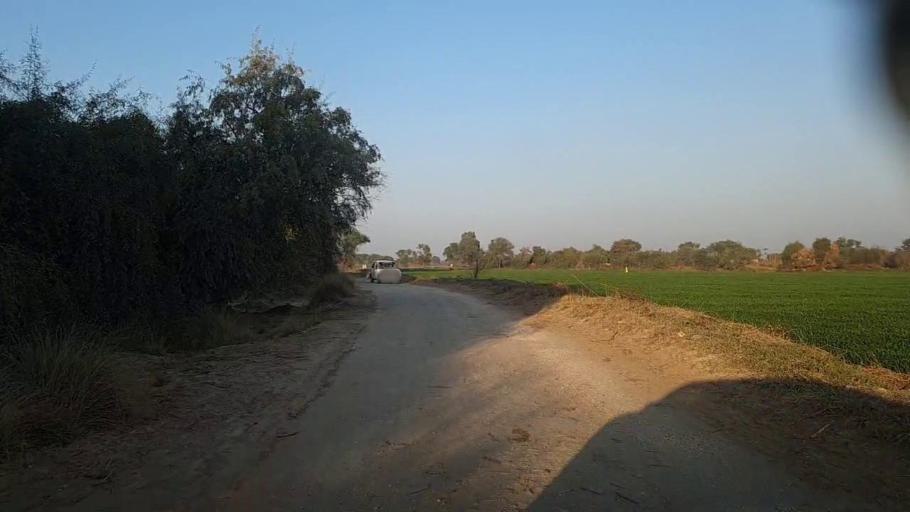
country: PK
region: Sindh
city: Mirpur Mathelo
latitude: 27.8877
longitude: 69.6547
